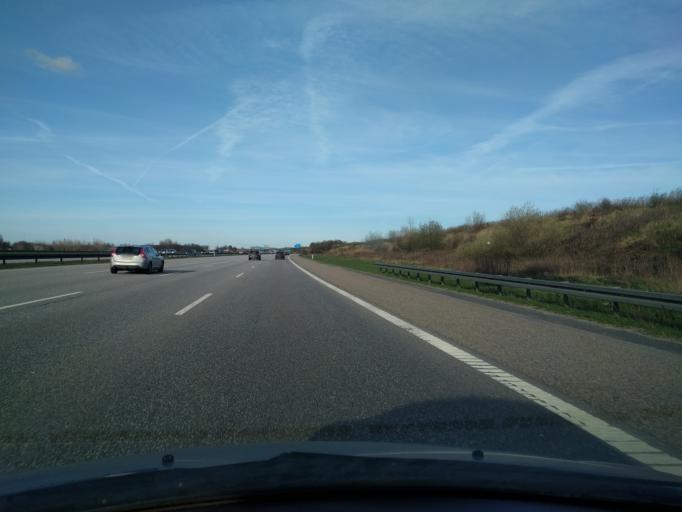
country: DK
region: Zealand
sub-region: Greve Kommune
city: Greve
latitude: 55.5957
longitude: 12.2850
